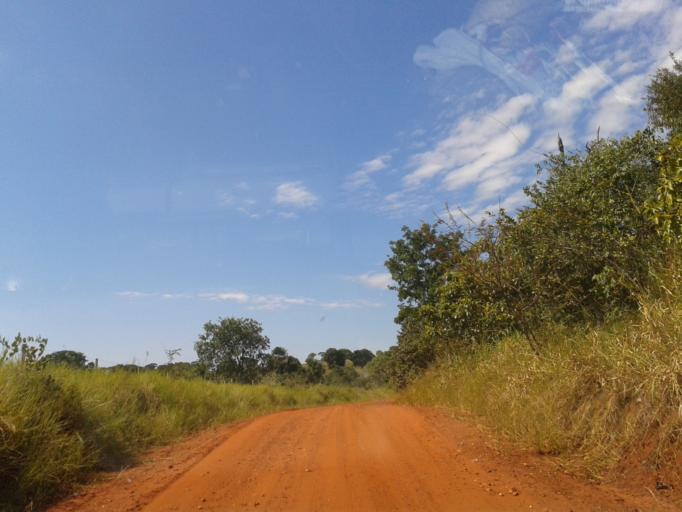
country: BR
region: Minas Gerais
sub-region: Campina Verde
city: Campina Verde
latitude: -19.4012
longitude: -49.7611
